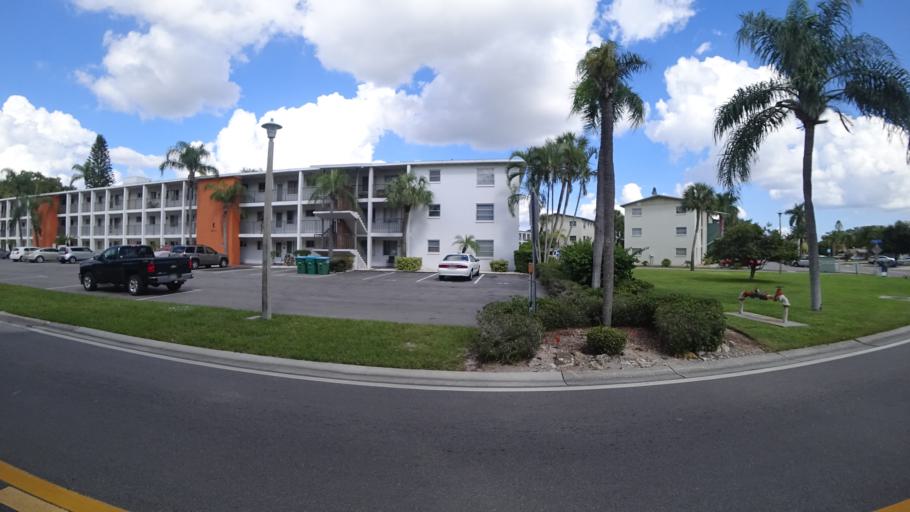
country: US
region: Florida
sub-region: Manatee County
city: Bayshore Gardens
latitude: 27.4351
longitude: -82.5867
